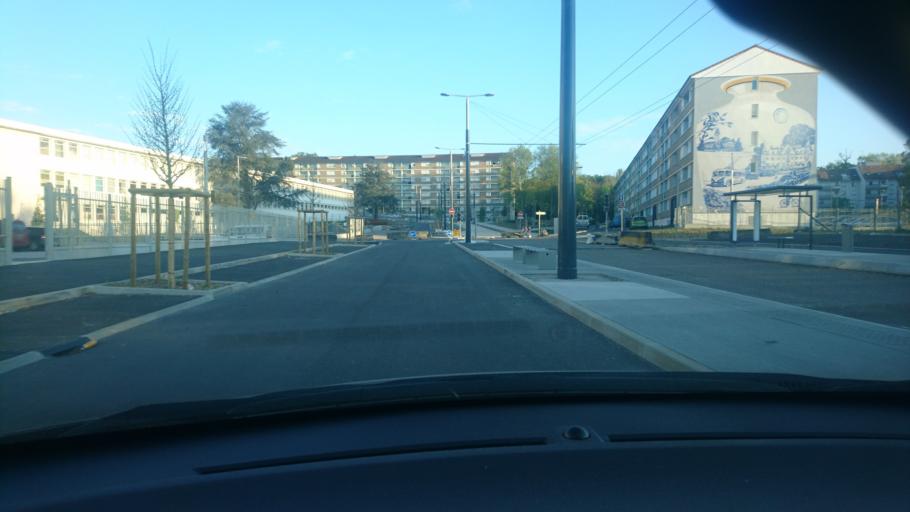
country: FR
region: Limousin
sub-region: Departement de la Haute-Vienne
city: Limoges
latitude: 45.8552
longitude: 1.2738
